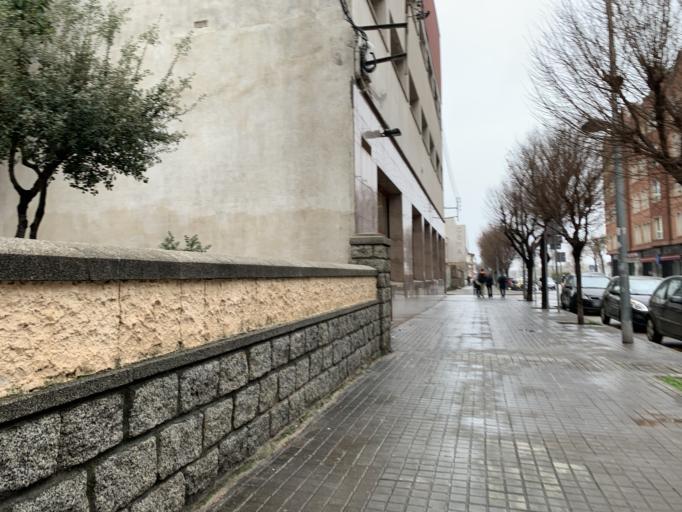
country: ES
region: Catalonia
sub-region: Provincia de Barcelona
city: Mataro
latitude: 41.5320
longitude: 2.4378
